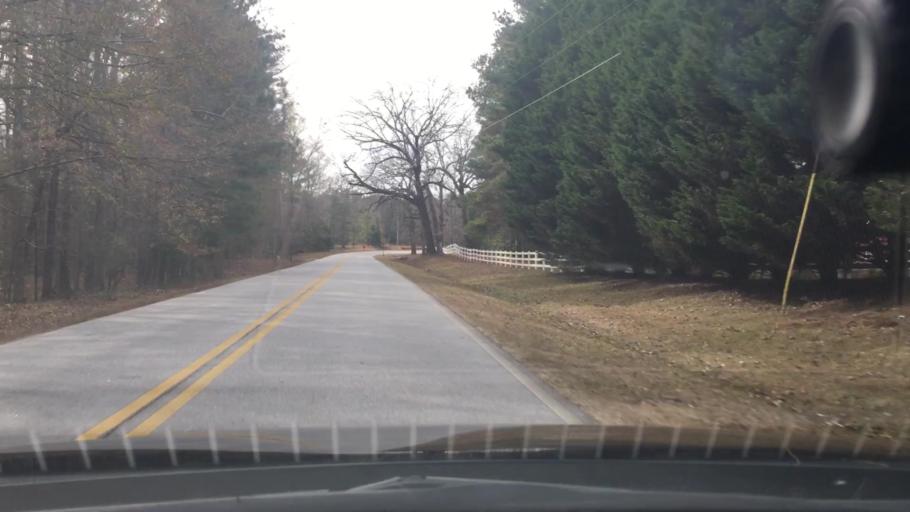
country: US
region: Georgia
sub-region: Spalding County
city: Experiment
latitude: 33.2788
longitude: -84.4159
